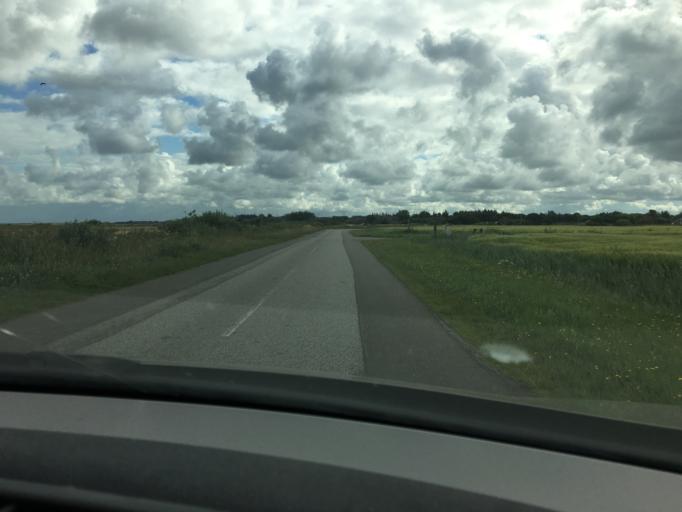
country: DK
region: South Denmark
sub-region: Varde Kommune
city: Oksbol
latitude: 55.8355
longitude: 8.2595
